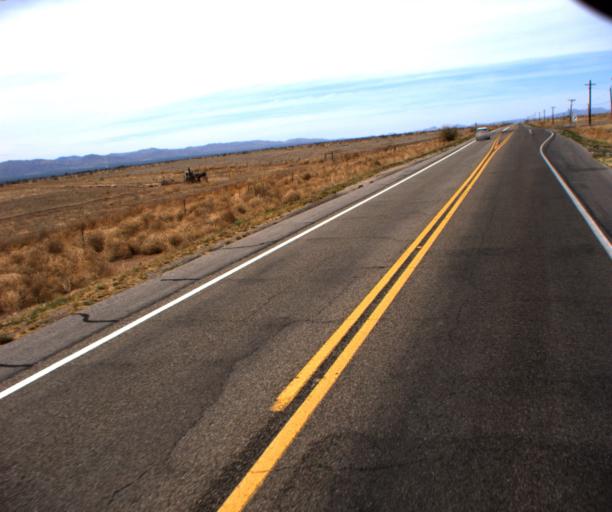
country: US
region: Arizona
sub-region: Cochise County
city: Pirtleville
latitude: 31.4443
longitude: -109.5989
